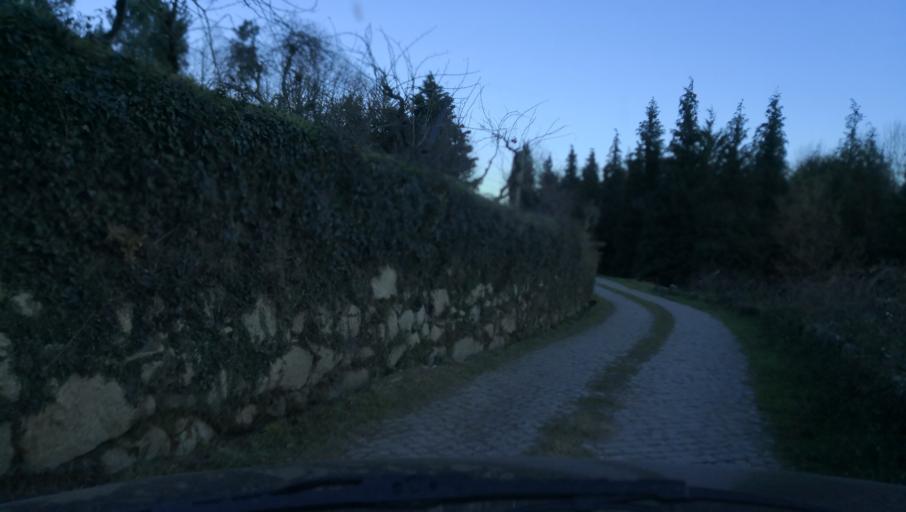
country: PT
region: Vila Real
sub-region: Vila Real
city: Vila Real
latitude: 41.3033
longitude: -7.7773
